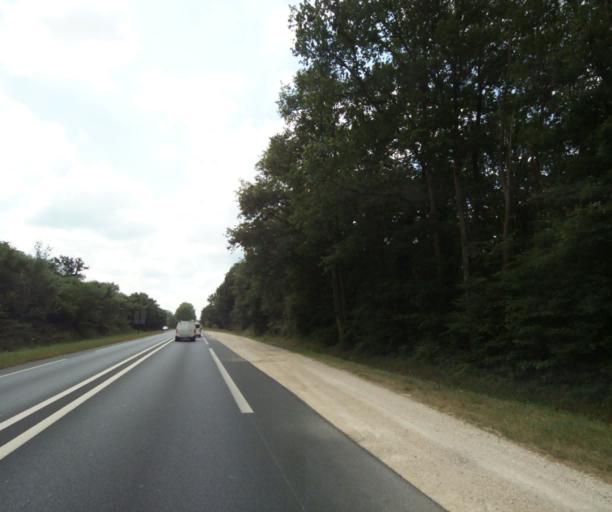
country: FR
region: Centre
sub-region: Departement du Loiret
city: Saint-Cyr-en-Val
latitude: 47.8214
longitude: 1.9242
